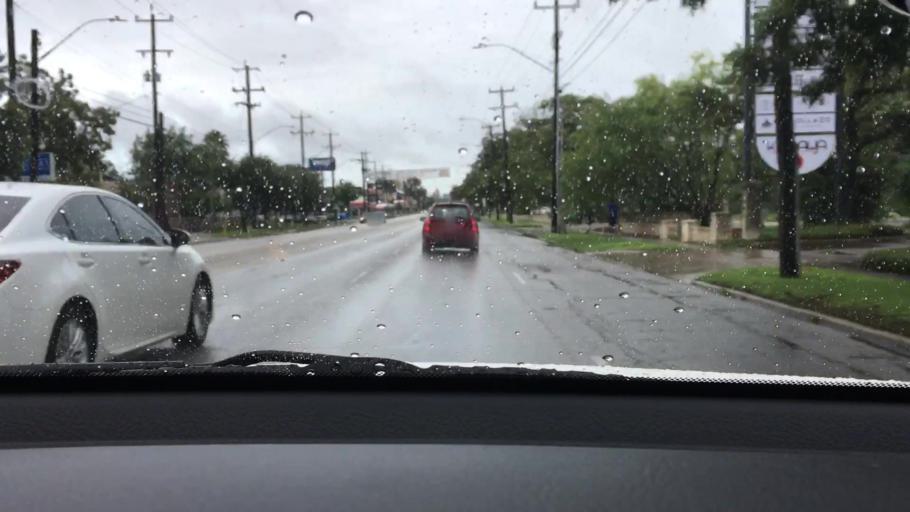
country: US
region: Texas
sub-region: Bexar County
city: Terrell Hills
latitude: 29.4634
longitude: -98.4653
